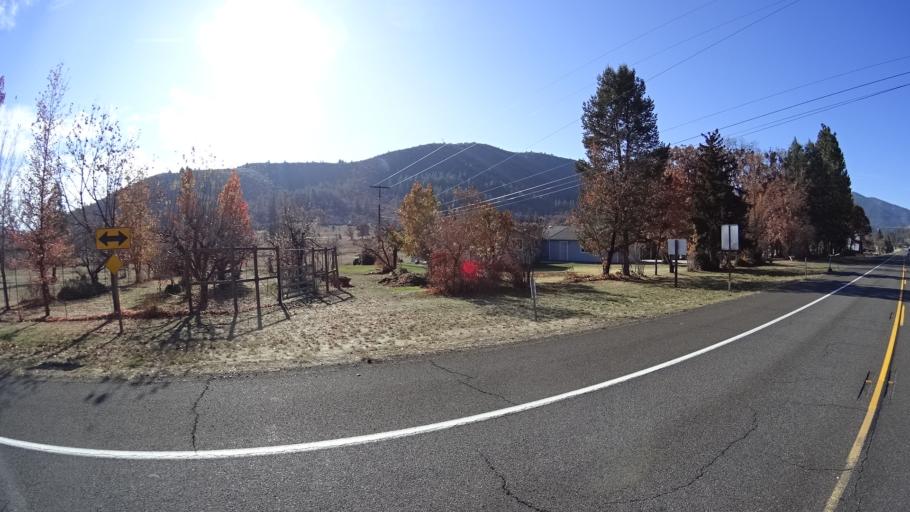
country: US
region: California
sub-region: Siskiyou County
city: Yreka
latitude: 41.6913
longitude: -122.6555
